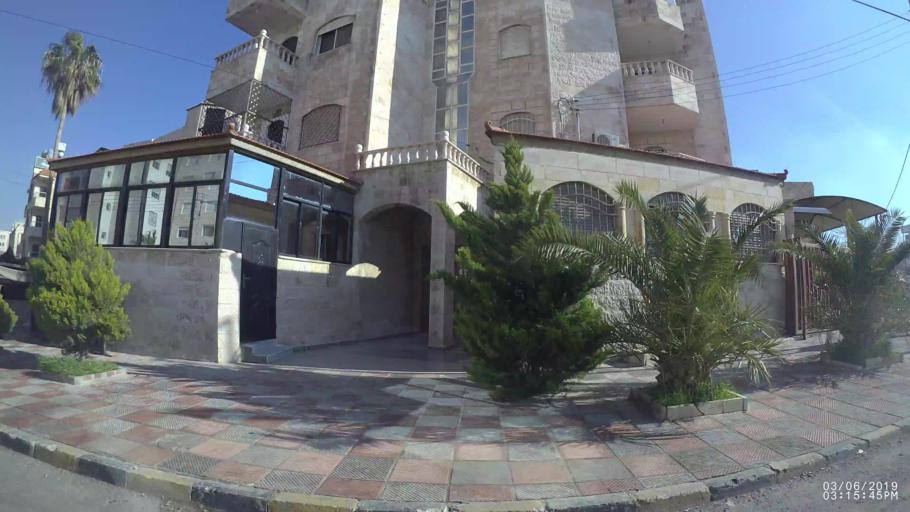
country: JO
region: Amman
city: Amman
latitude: 31.9870
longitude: 35.9324
